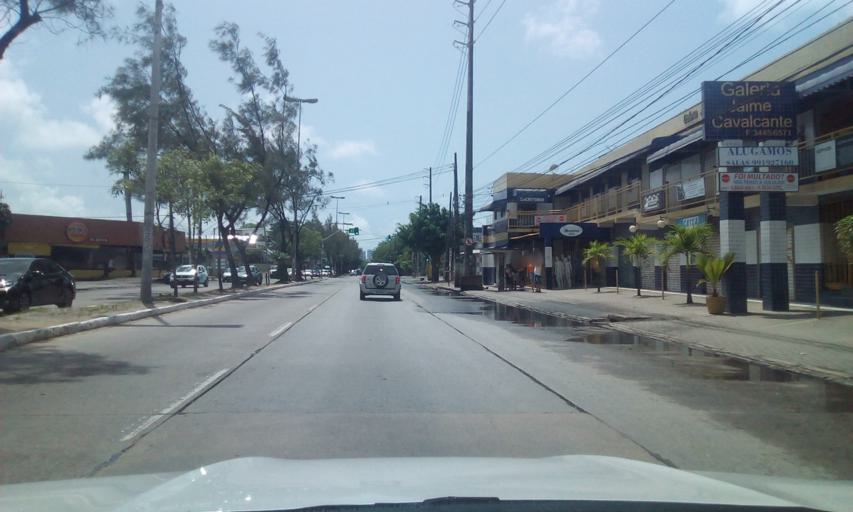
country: BR
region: Pernambuco
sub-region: Recife
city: Recife
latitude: -8.0631
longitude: -34.9332
